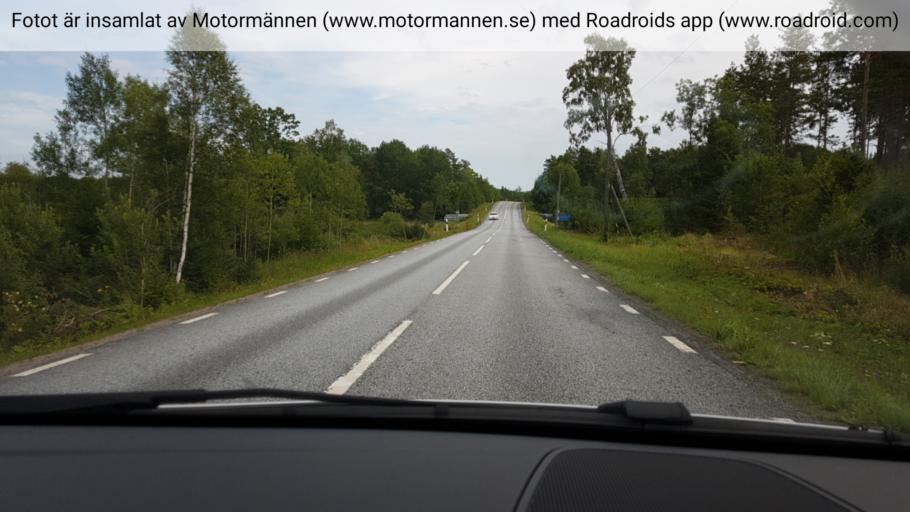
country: SE
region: Stockholm
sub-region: Norrtalje Kommun
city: Hallstavik
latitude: 60.0944
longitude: 18.4759
